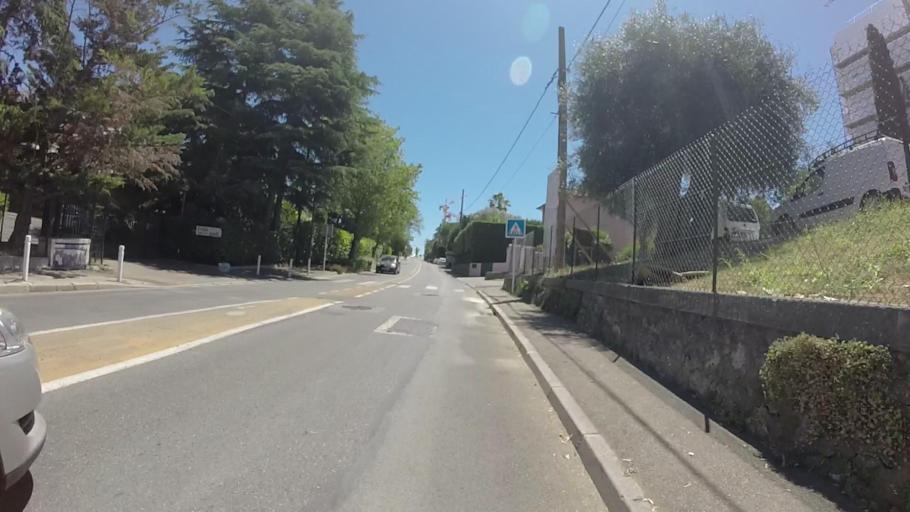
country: FR
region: Provence-Alpes-Cote d'Azur
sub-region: Departement des Alpes-Maritimes
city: Antibes
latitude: 43.5844
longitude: 7.1039
